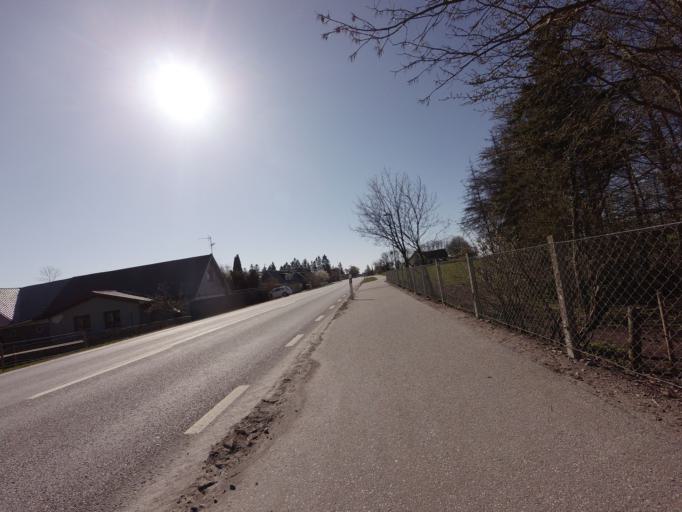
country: SE
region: Skane
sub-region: Malmo
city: Oxie
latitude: 55.4837
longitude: 13.1257
